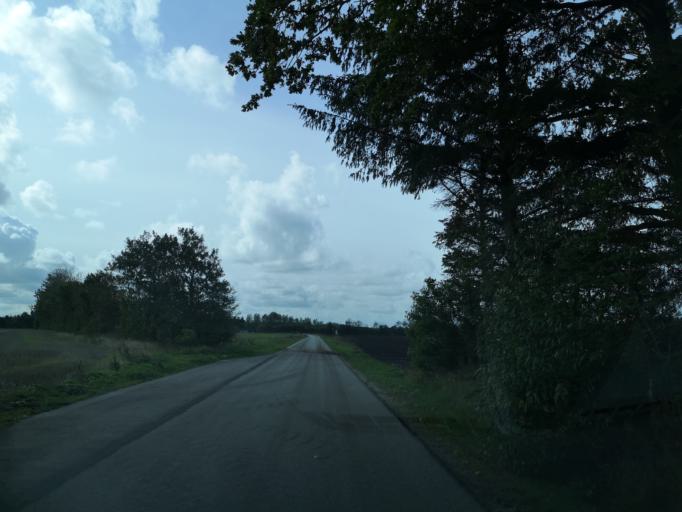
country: DK
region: Central Jutland
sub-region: Ringkobing-Skjern Kommune
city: Skjern
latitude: 55.9459
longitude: 8.5343
